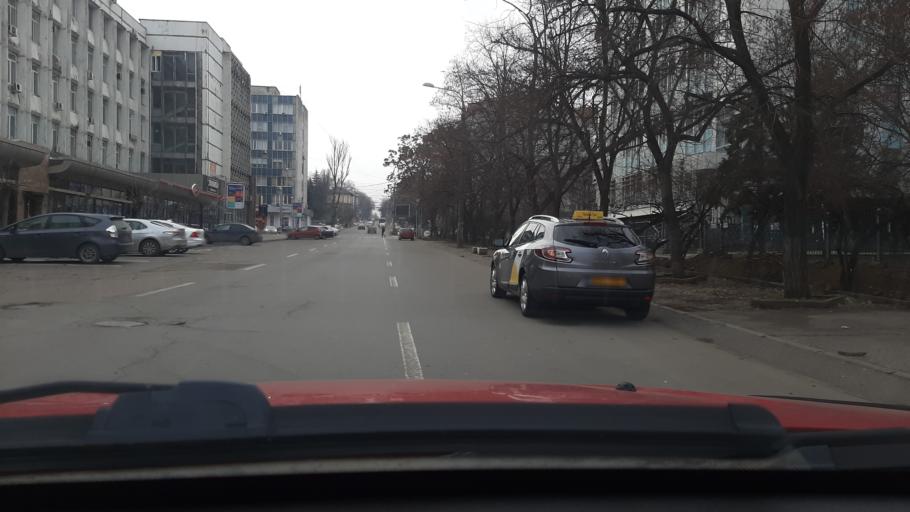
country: MD
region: Chisinau
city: Chisinau
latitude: 47.0303
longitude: 28.8378
